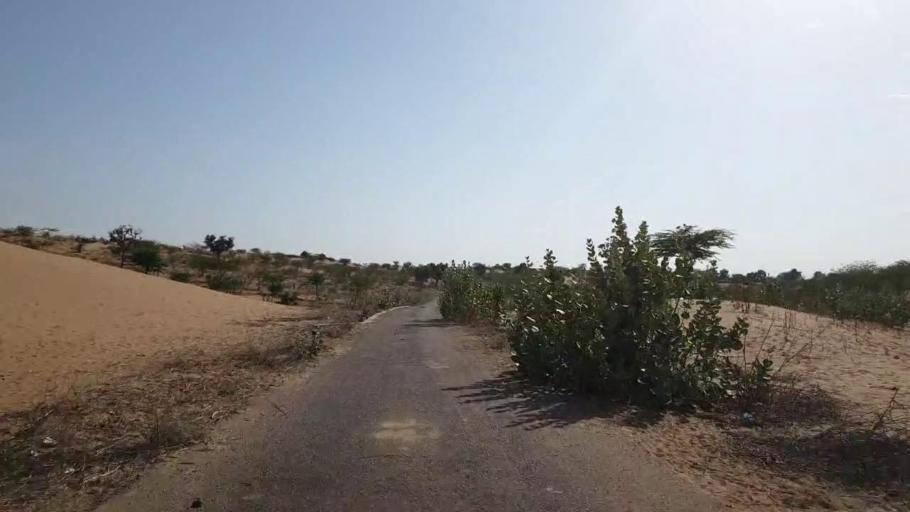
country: PK
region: Sindh
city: Nabisar
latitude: 25.0480
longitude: 70.0207
